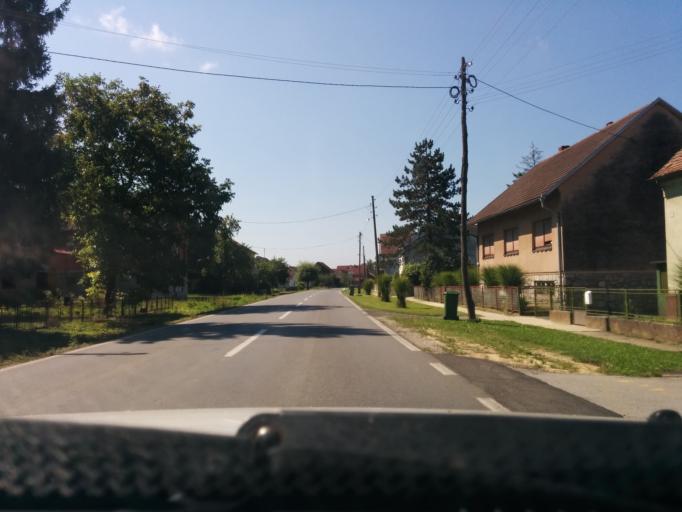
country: HR
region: Sisacko-Moslavacka
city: Lipovljani
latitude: 45.4228
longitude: 16.9042
